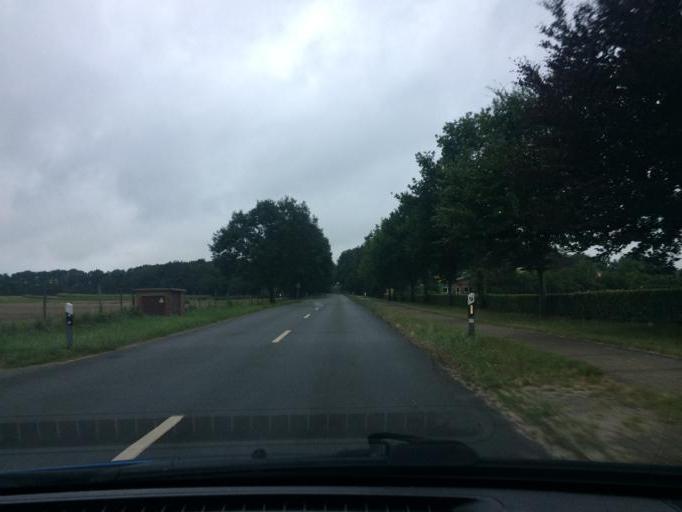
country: DE
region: Lower Saxony
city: Soderstorf
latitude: 53.1450
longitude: 10.1492
